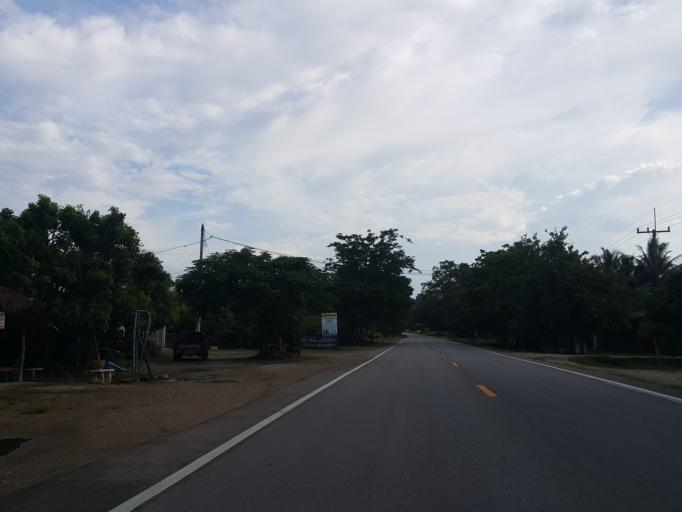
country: TH
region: Chiang Mai
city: Phrao
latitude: 19.2366
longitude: 99.1861
